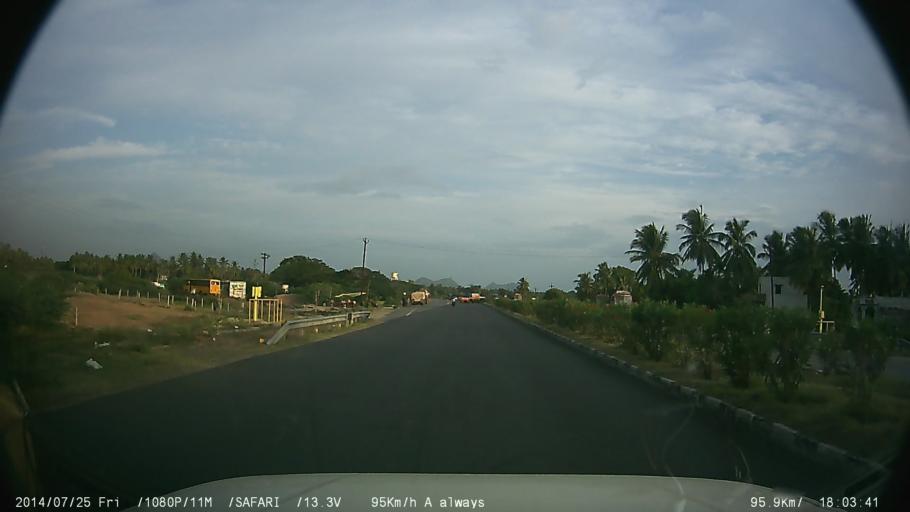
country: IN
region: Tamil Nadu
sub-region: Krishnagiri
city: Kaverippattanam
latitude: 12.4587
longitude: 78.2154
